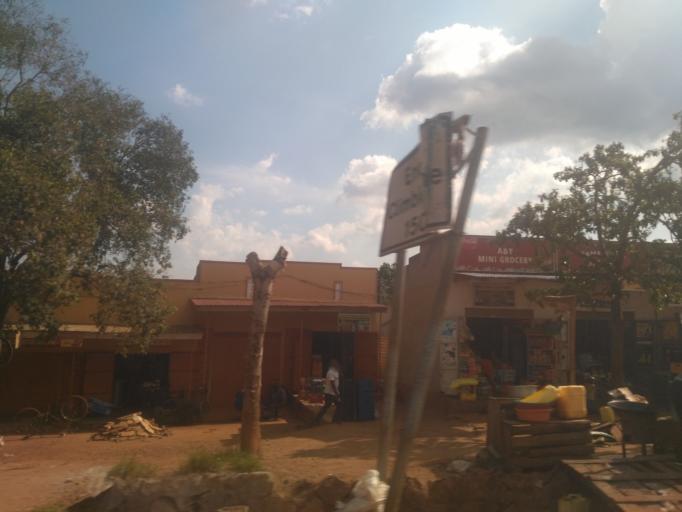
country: UG
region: Central Region
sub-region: Wakiso District
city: Kajansi
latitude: 0.2787
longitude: 32.4790
